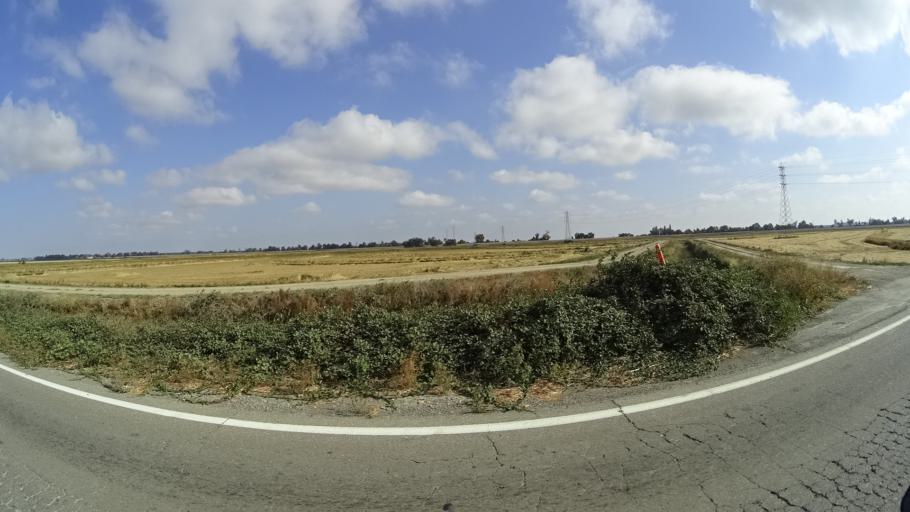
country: US
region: California
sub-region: Yolo County
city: Woodland
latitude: 38.8141
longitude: -121.7381
